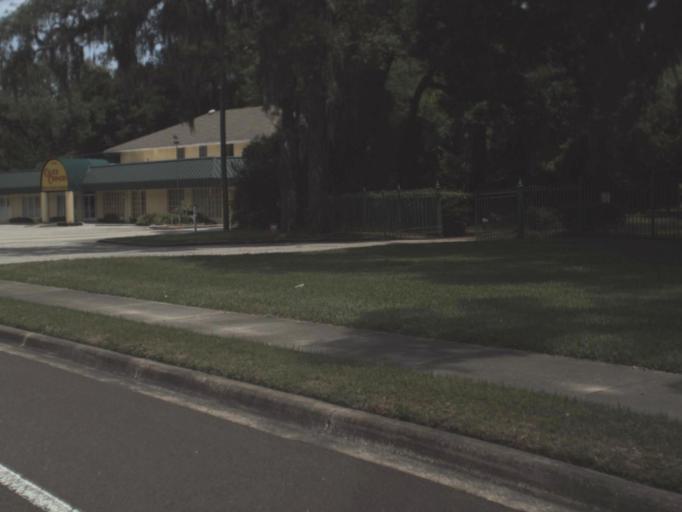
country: US
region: Florida
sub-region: Duval County
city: Jacksonville
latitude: 30.2706
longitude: -81.6485
